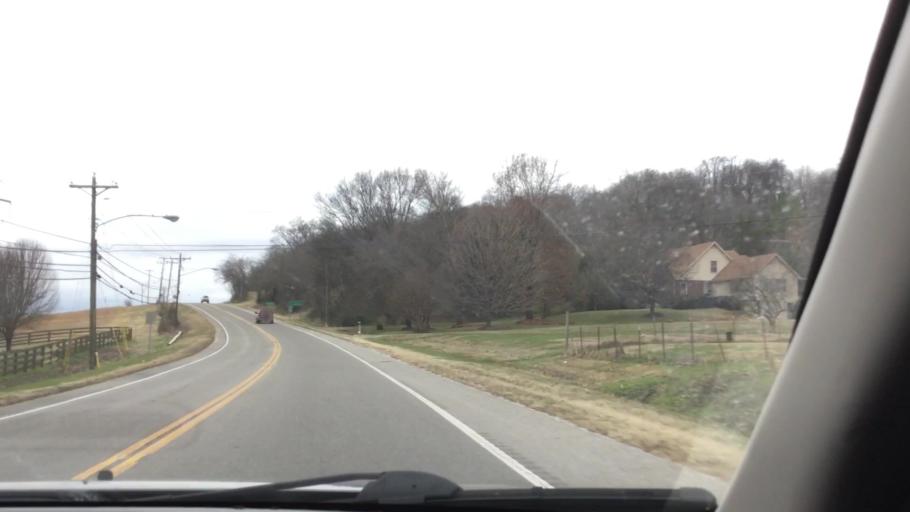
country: US
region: Tennessee
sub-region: Maury County
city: Columbia
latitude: 35.6251
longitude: -87.0962
